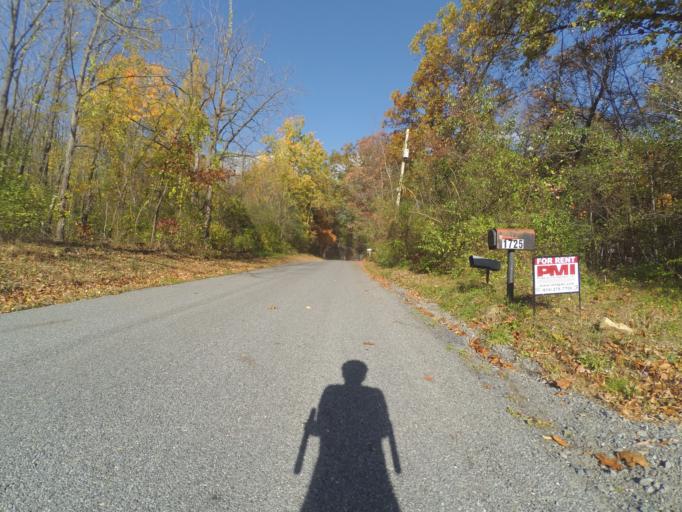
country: US
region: Pennsylvania
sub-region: Centre County
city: Houserville
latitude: 40.8666
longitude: -77.8198
